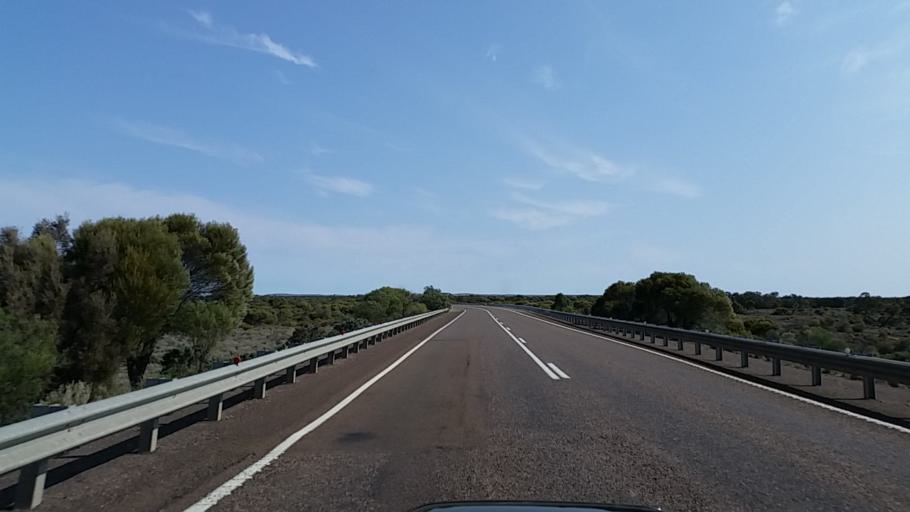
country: AU
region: South Australia
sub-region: Whyalla
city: Whyalla
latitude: -32.7054
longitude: 137.5068
